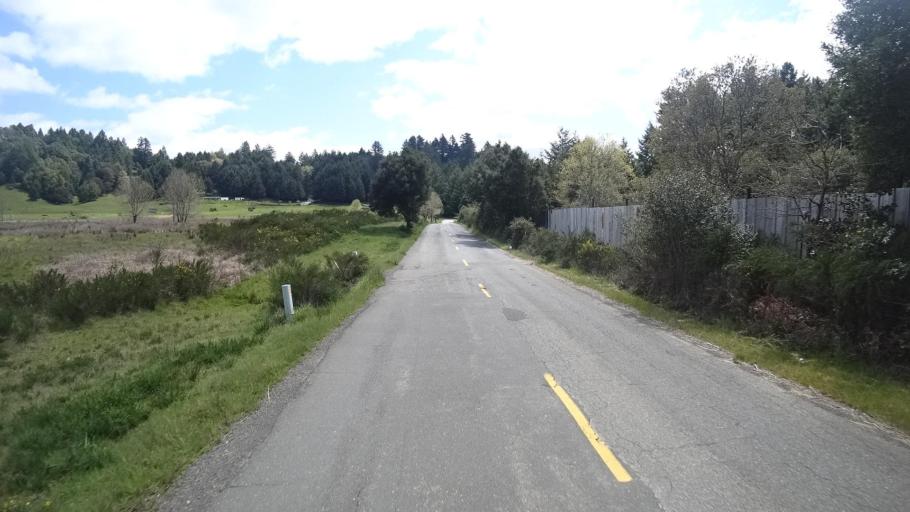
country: US
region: California
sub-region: Humboldt County
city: Redway
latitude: 40.0377
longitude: -123.9560
